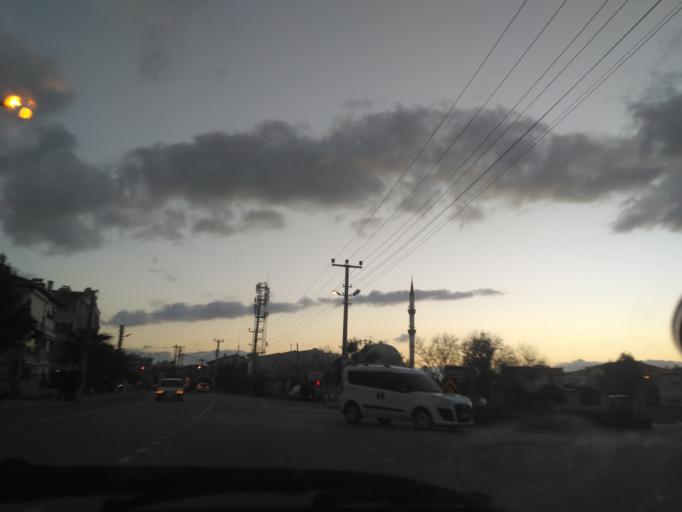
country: TR
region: Balikesir
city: Ayvalik
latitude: 39.2736
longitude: 26.6680
